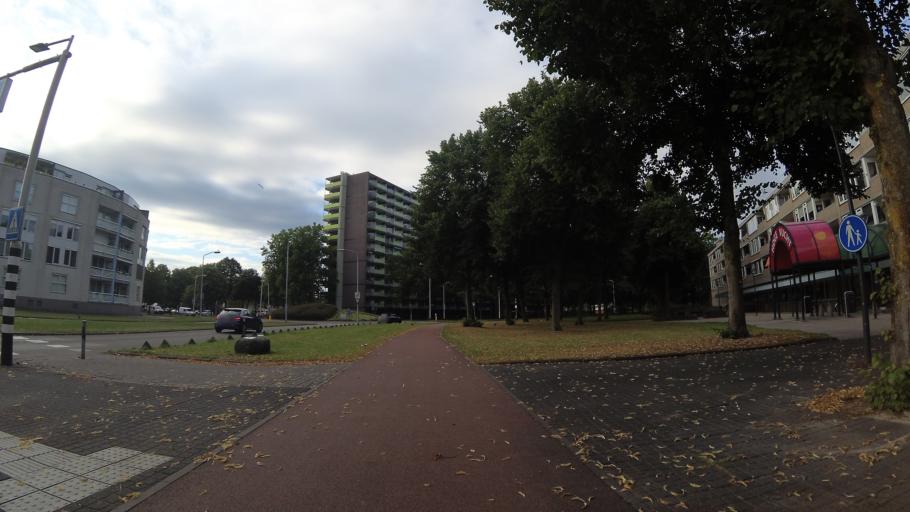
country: NL
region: North Brabant
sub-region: Gemeente Breda
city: Hoge Vucht
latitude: 51.6085
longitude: 4.7911
